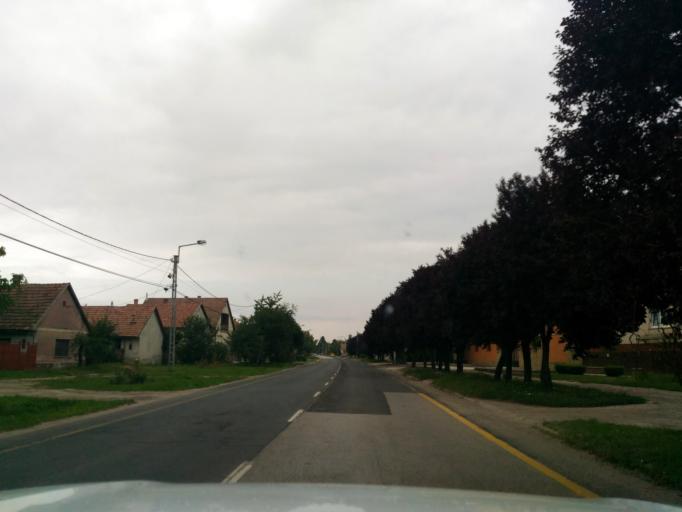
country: HU
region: Pest
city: Alsonemedi
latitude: 47.3075
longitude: 19.1761
